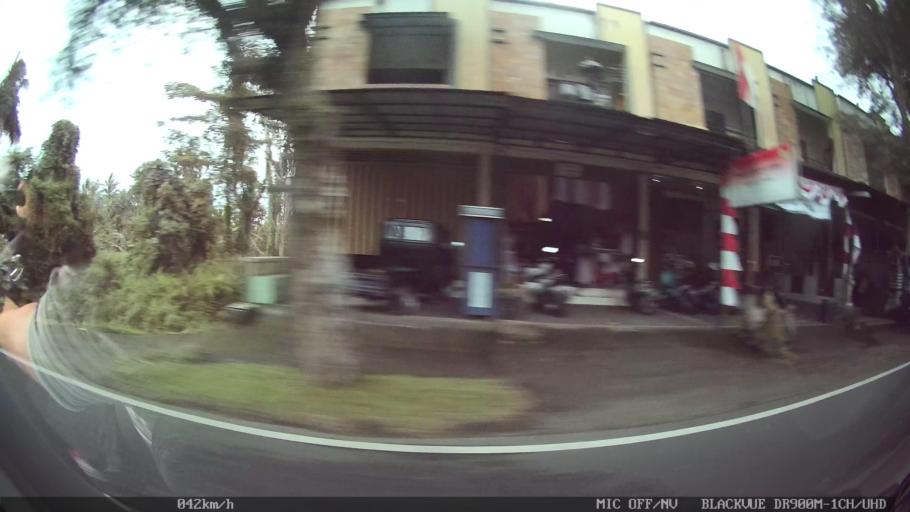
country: ID
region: Bali
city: Pohgending Kangin
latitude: -8.4292
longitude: 115.1439
